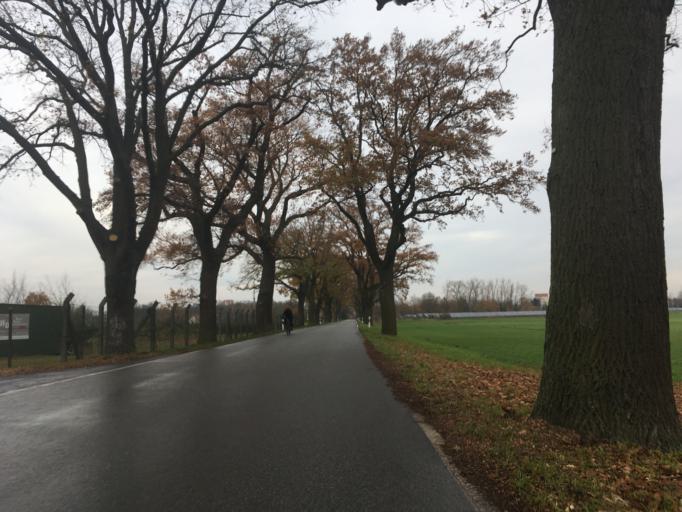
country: DE
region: Brandenburg
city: Letschin
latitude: 52.6950
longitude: 14.4042
